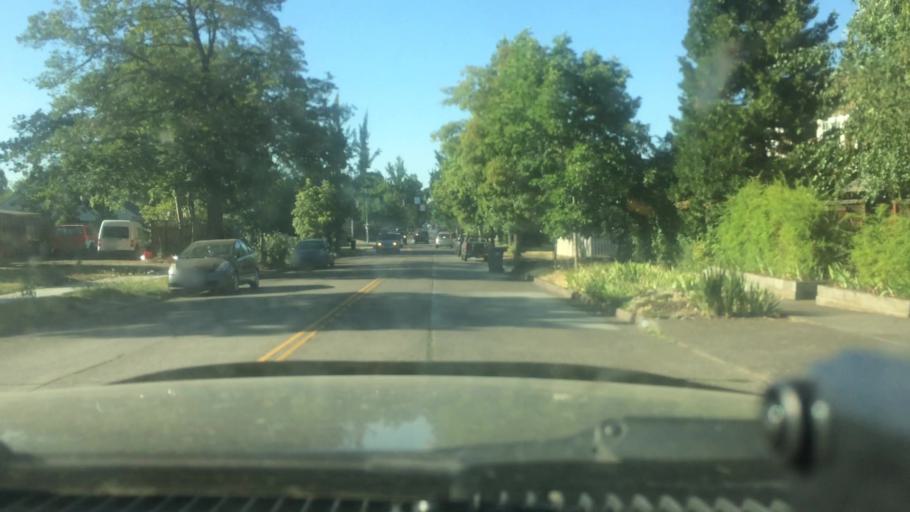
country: US
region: Oregon
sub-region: Lane County
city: Eugene
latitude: 44.0392
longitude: -123.1013
